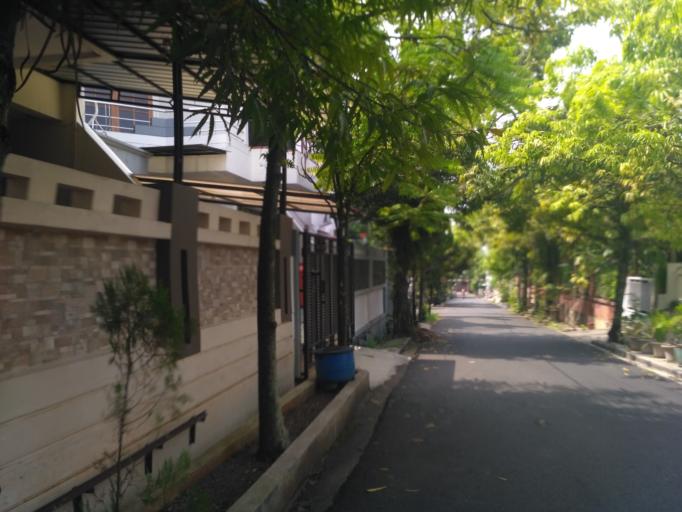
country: ID
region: Central Java
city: Semarang
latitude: -7.0480
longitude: 110.4254
